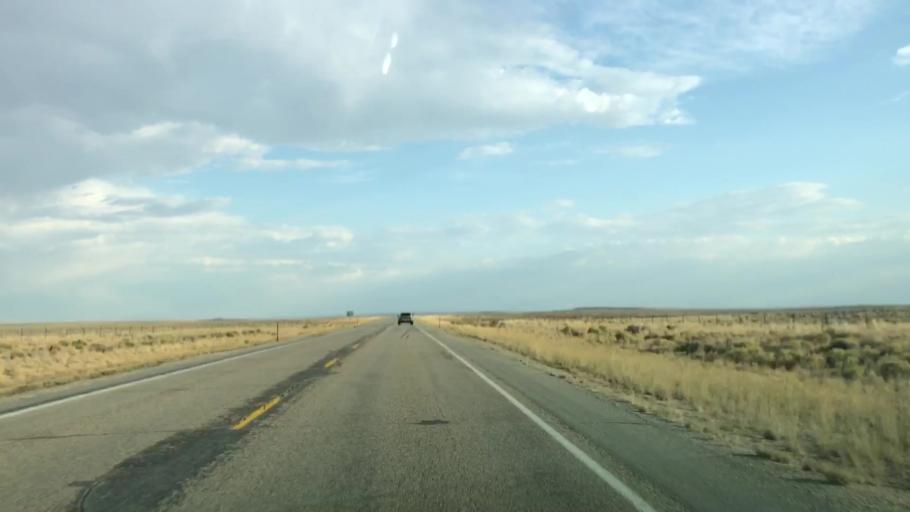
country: US
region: Wyoming
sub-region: Sublette County
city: Pinedale
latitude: 42.3982
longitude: -109.5449
